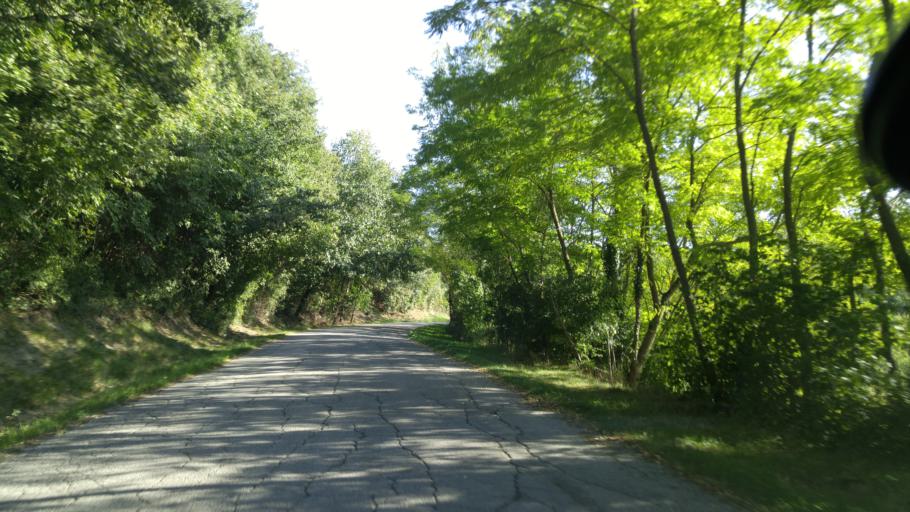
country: IT
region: The Marches
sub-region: Provincia di Pesaro e Urbino
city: Fermignano
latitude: 43.6620
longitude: 12.6504
